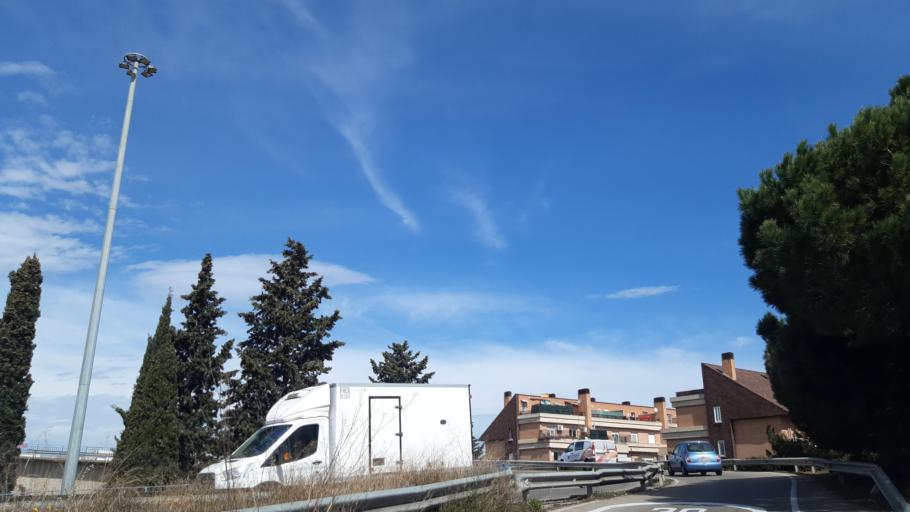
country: ES
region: Aragon
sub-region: Provincia de Zaragoza
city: Utebo
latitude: 41.7041
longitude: -1.0038
